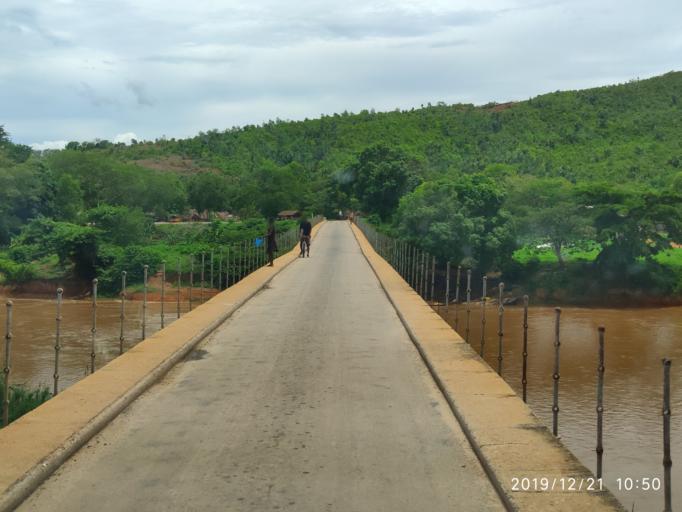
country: MG
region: Diana
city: Ambarakaraka
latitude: -13.3701
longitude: 48.8723
